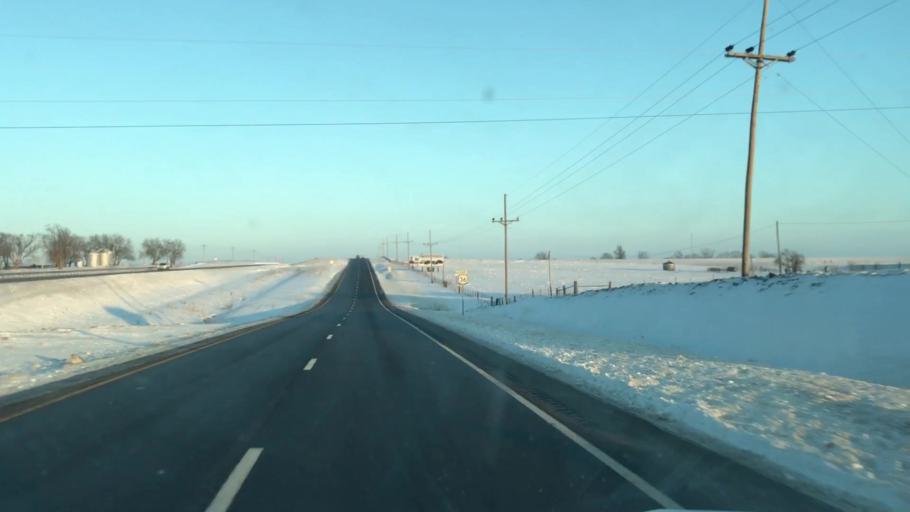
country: US
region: Missouri
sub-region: Clinton County
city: Cameron
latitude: 39.7541
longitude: -94.2810
